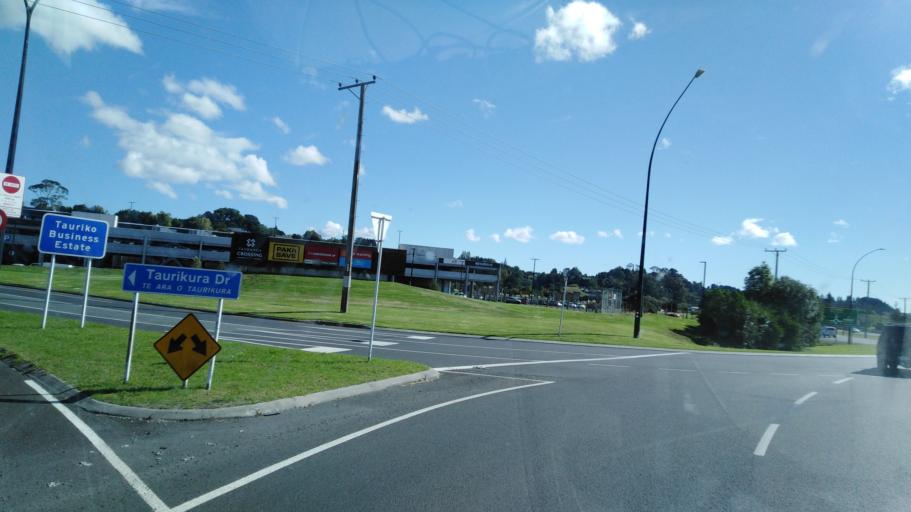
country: NZ
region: Bay of Plenty
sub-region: Tauranga City
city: Tauranga
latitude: -37.7386
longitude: 176.1076
